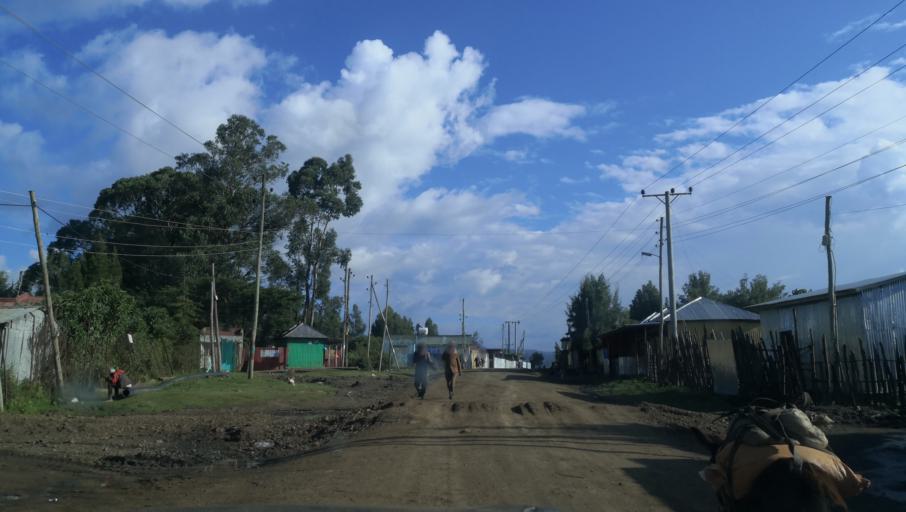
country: ET
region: Oromiya
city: Tulu Bolo
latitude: 8.4634
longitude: 38.2524
